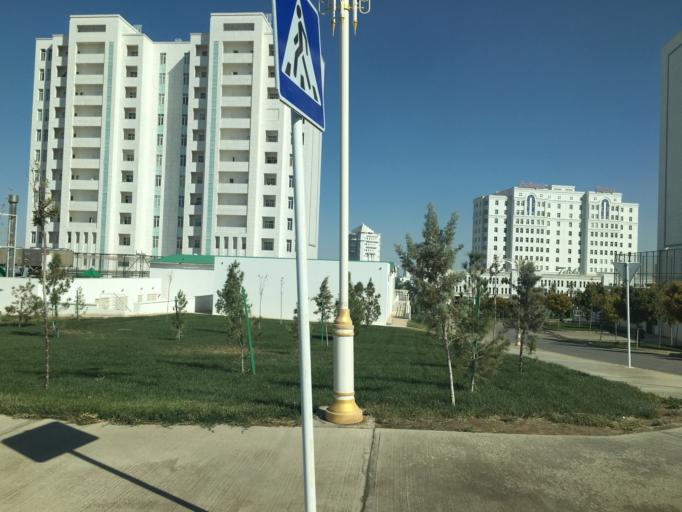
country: TM
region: Ahal
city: Ashgabat
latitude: 37.9362
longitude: 58.3630
